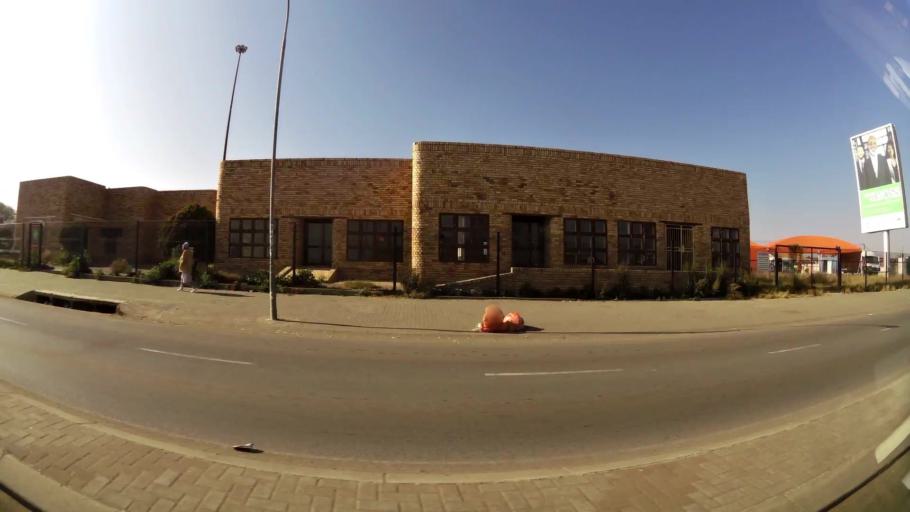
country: ZA
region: Orange Free State
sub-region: Mangaung Metropolitan Municipality
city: Bloemfontein
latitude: -29.1628
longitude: 26.2381
